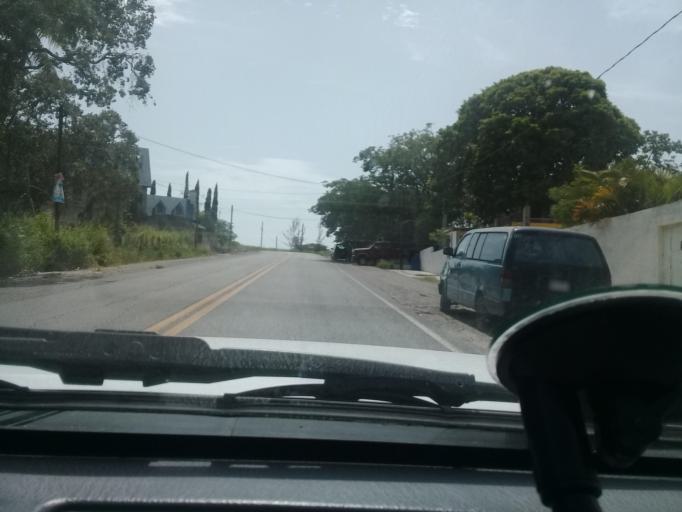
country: MX
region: Veracruz
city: Villa Cuauhtemoc
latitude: 22.2127
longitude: -97.8276
